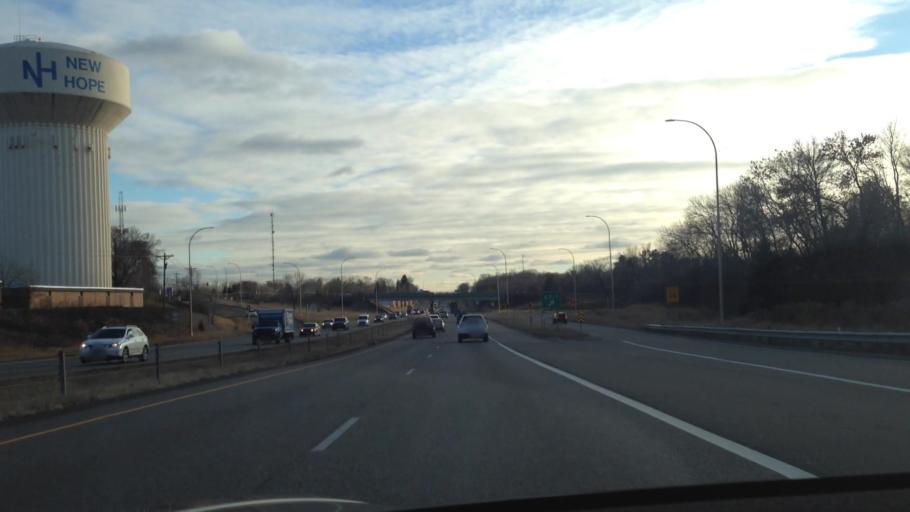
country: US
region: Minnesota
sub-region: Hennepin County
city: New Hope
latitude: 45.0107
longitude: -93.4010
